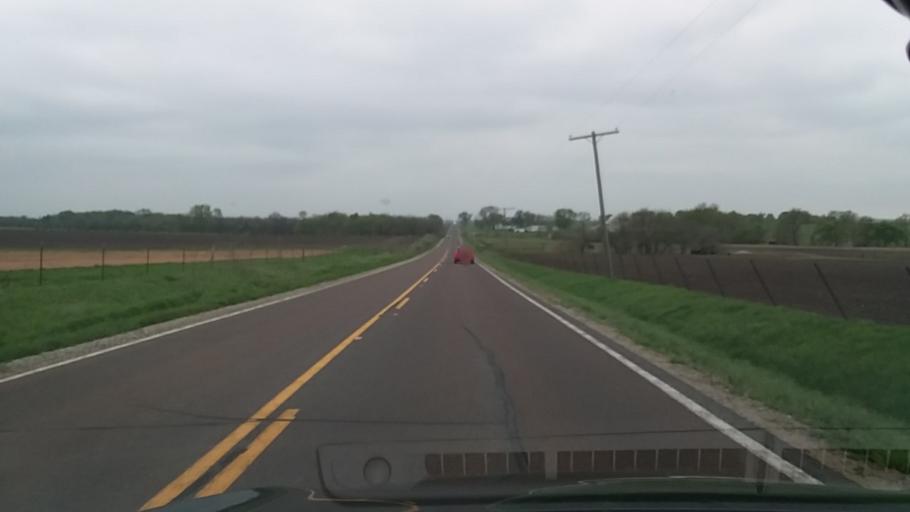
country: US
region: Kansas
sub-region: Douglas County
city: Eudora
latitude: 38.8949
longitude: -95.0934
